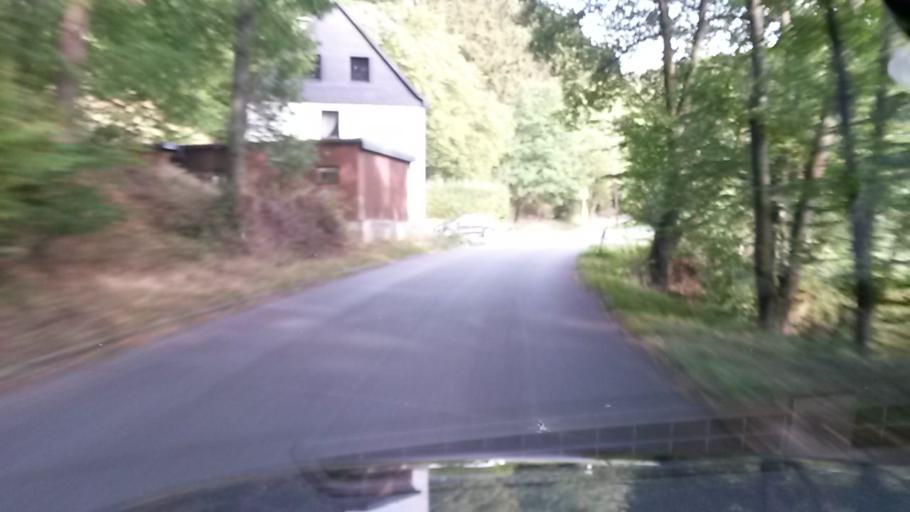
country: DE
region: North Rhine-Westphalia
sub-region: Regierungsbezirk Arnsberg
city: Herscheid
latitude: 51.2244
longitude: 7.7318
